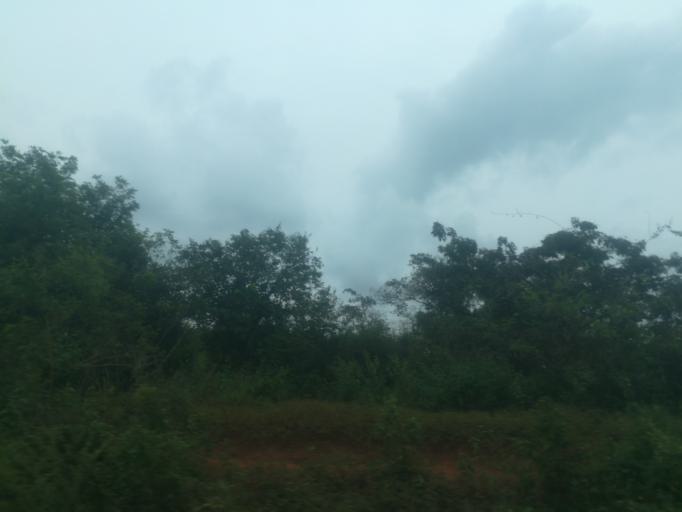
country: NG
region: Ogun
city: Ayetoro
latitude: 7.1092
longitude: 3.1344
